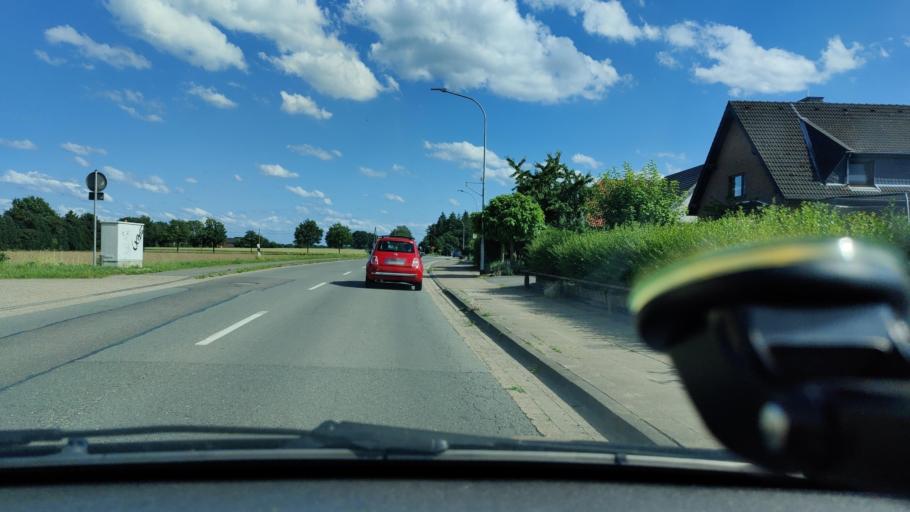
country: DE
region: North Rhine-Westphalia
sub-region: Regierungsbezirk Dusseldorf
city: Alpen
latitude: 51.5705
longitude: 6.5234
